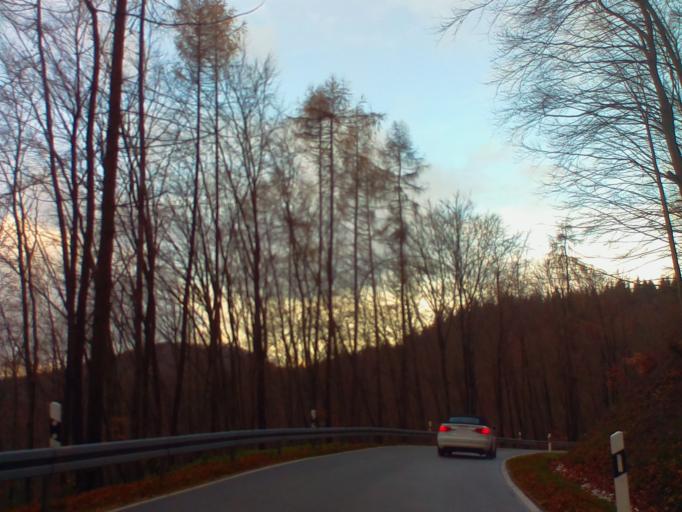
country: DE
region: Hesse
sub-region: Regierungsbezirk Darmstadt
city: Birkenau
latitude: 49.5399
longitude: 8.7158
